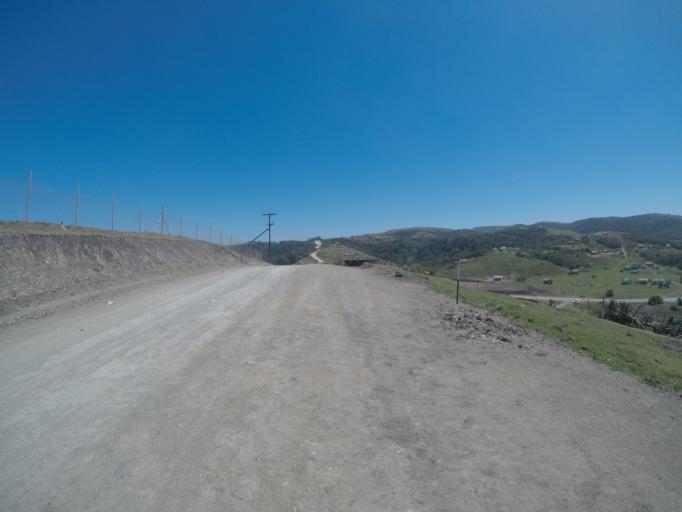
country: ZA
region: Eastern Cape
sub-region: OR Tambo District Municipality
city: Libode
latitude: -32.0335
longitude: 29.1064
